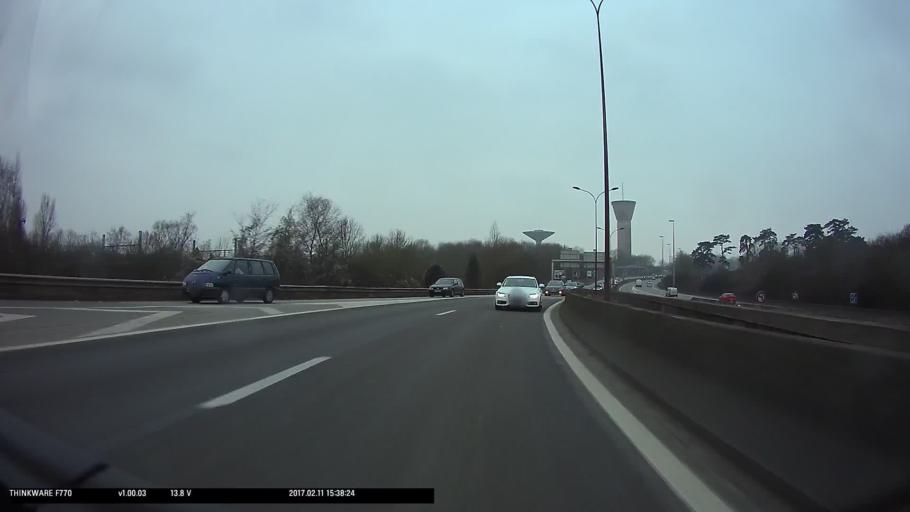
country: FR
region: Ile-de-France
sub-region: Departement des Yvelines
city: Montigny-le-Bretonneux
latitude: 48.7835
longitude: 2.0336
